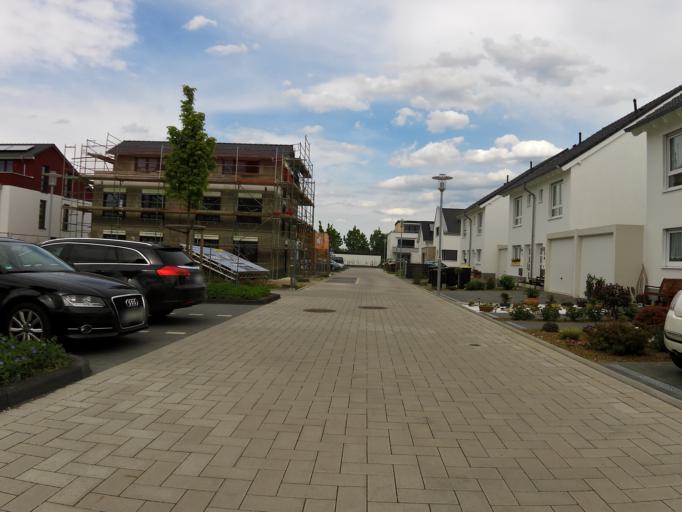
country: DE
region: North Rhine-Westphalia
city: Meckenheim
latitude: 50.6282
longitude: 7.0146
